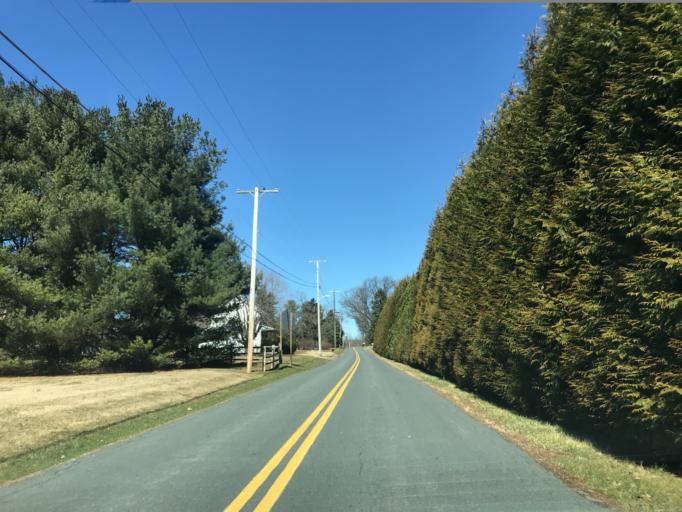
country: US
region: Pennsylvania
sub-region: York County
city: New Freedom
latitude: 39.6901
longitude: -76.6885
